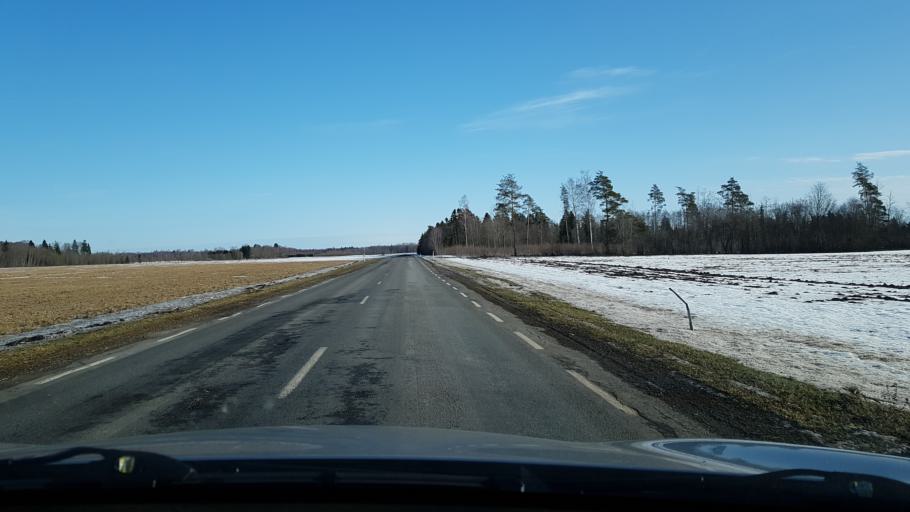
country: EE
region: Viljandimaa
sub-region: Vohma linn
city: Vohma
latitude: 58.6373
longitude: 25.6592
